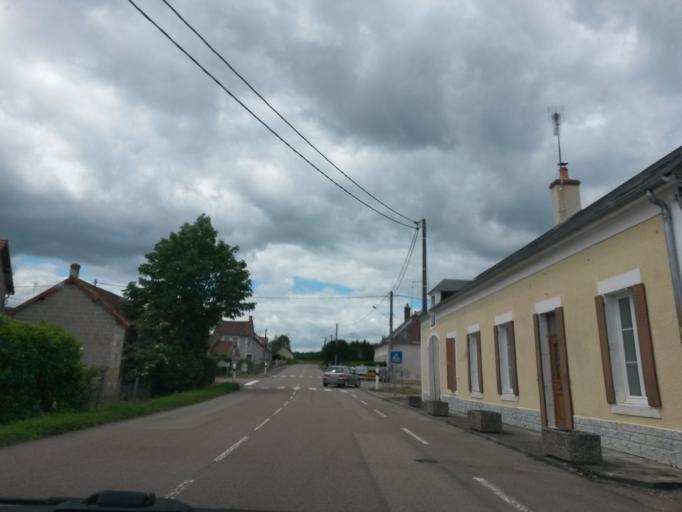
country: FR
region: Bourgogne
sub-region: Departement de la Nievre
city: Premery
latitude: 47.1935
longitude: 3.2225
